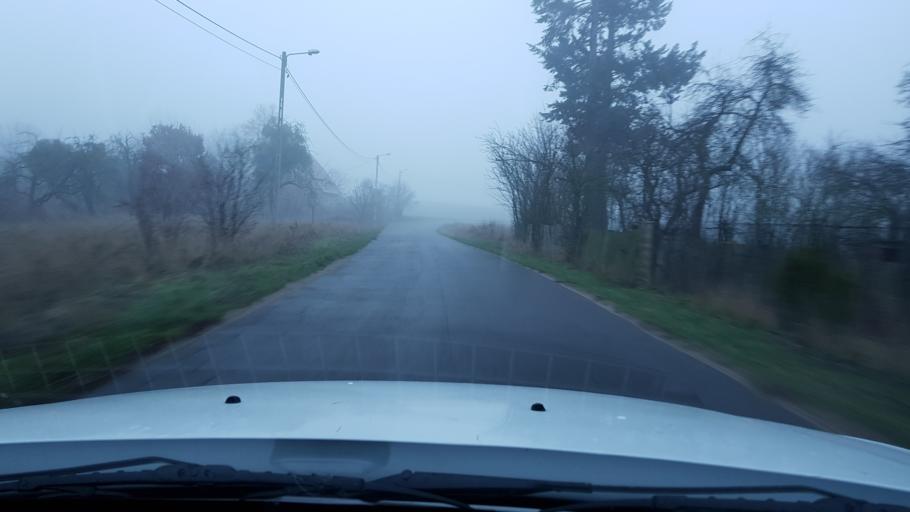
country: PL
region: West Pomeranian Voivodeship
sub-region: Powiat mysliborski
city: Mysliborz
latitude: 52.9043
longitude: 14.8221
